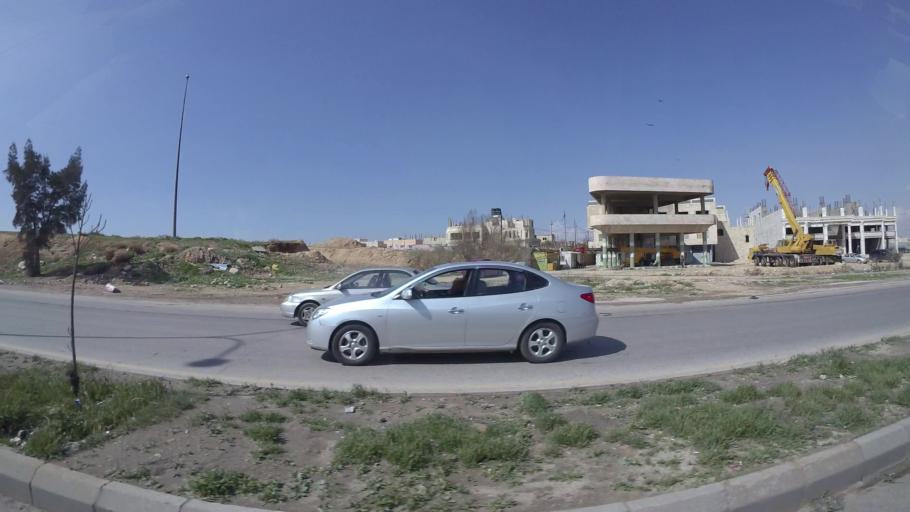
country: JO
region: Zarqa
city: Russeifa
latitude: 32.0199
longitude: 36.0793
